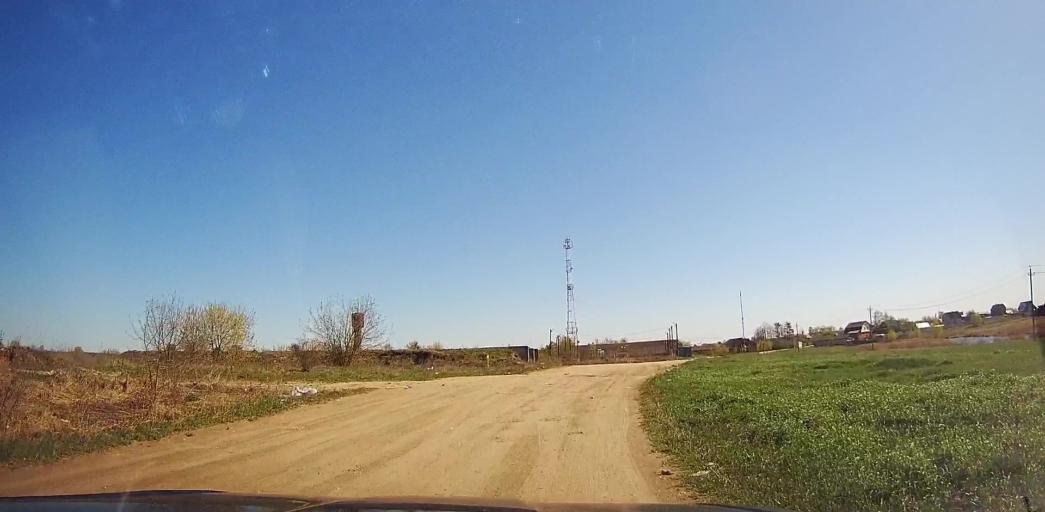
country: RU
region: Moskovskaya
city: Ramenskoye
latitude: 55.5558
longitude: 38.2859
